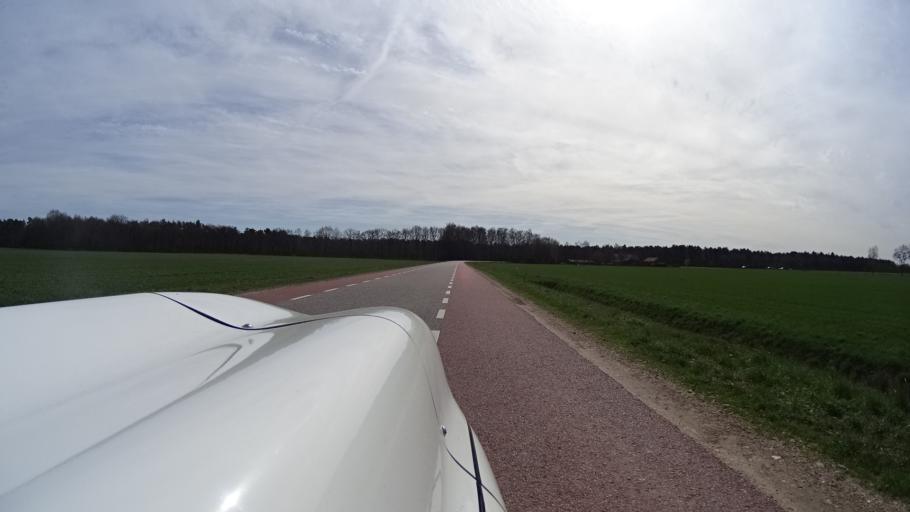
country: NL
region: Limburg
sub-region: Gemeente Venlo
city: Arcen
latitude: 51.5148
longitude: 6.2045
